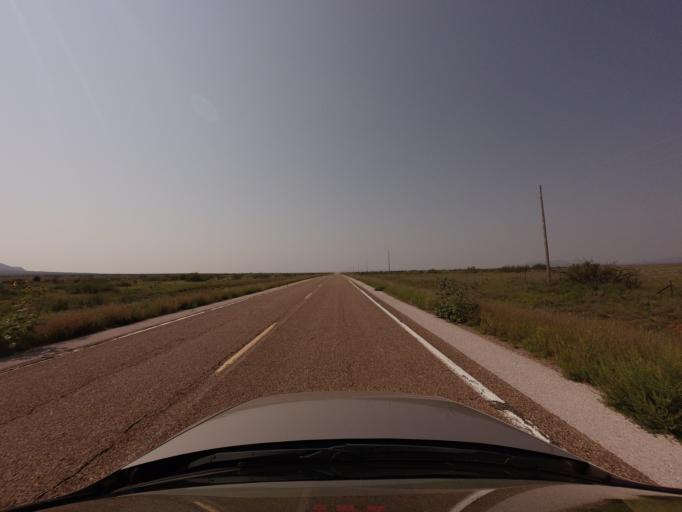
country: US
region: New Mexico
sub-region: Quay County
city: Tucumcari
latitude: 35.0063
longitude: -103.7420
